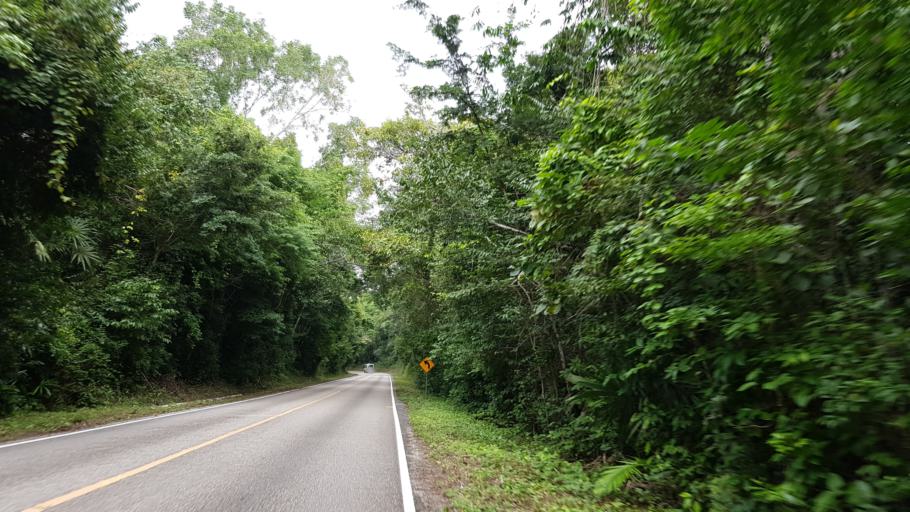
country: GT
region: Peten
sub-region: Municipio de San Jose
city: San Jose
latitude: 17.2099
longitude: -89.6182
